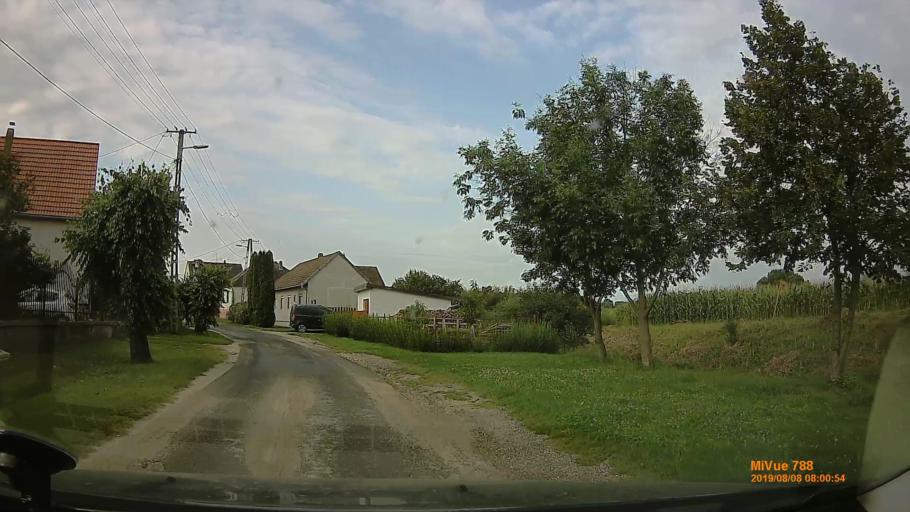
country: HU
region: Zala
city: Nagykanizsa
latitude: 46.4620
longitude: 16.9577
